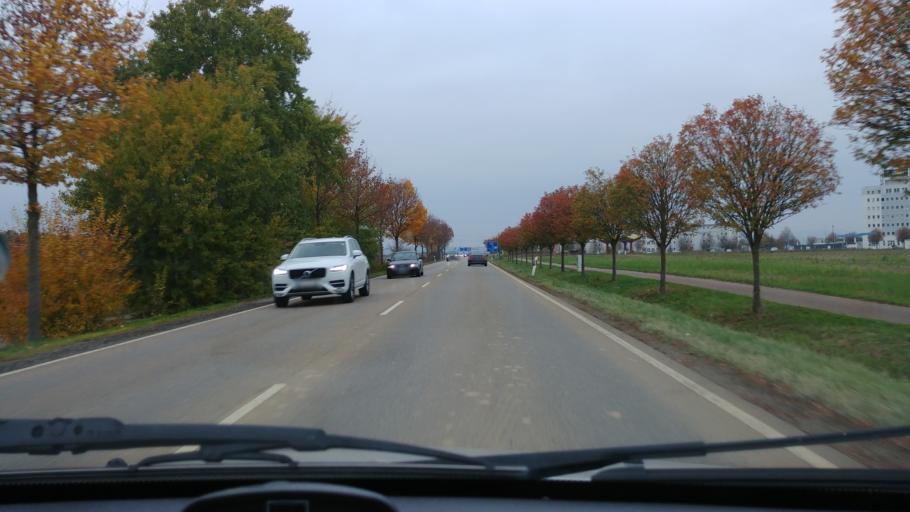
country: DE
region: Hesse
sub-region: Regierungsbezirk Giessen
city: Dehrn
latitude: 50.3785
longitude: 8.0957
